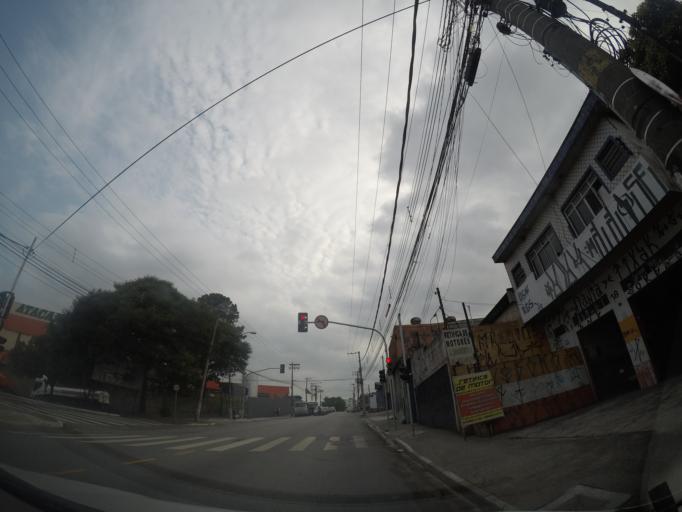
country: BR
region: Sao Paulo
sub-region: Guarulhos
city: Guarulhos
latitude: -23.4373
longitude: -46.5068
